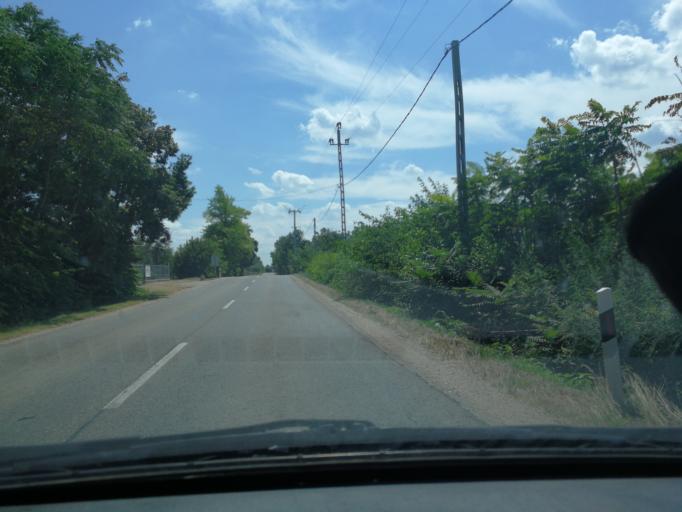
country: HU
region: Pest
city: Domsod
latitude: 47.0728
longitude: 19.0098
